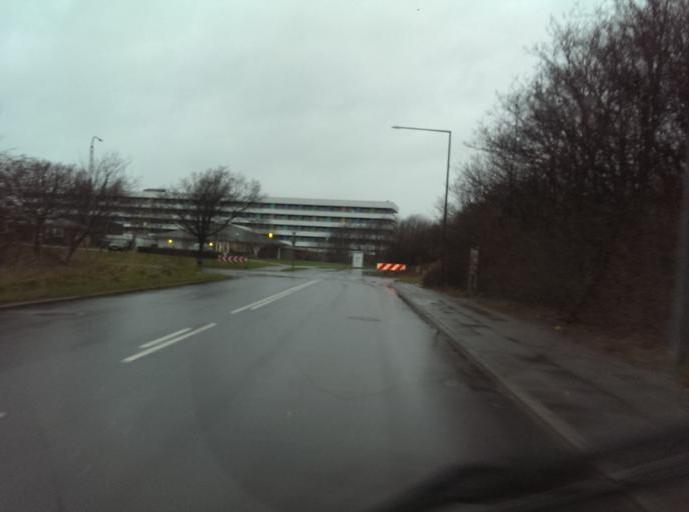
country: DK
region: South Denmark
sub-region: Esbjerg Kommune
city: Esbjerg
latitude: 55.4875
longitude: 8.4955
